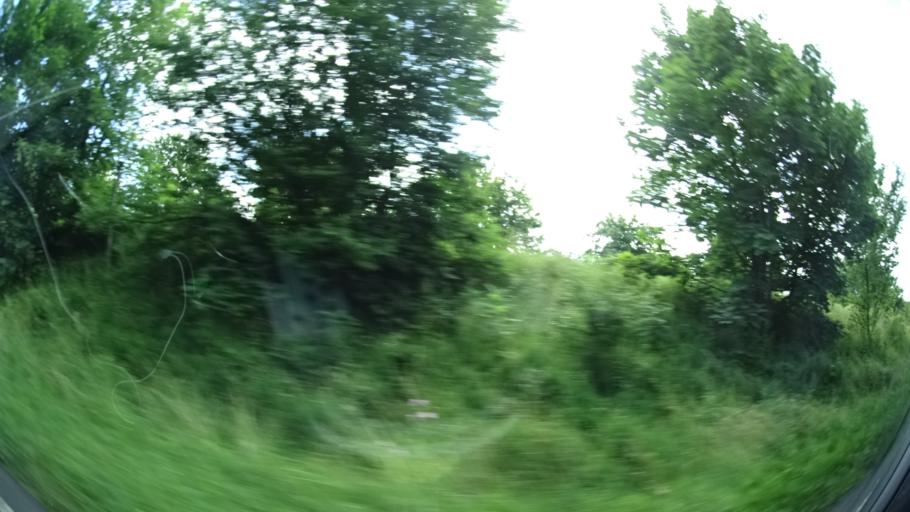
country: DK
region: Central Jutland
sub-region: Arhus Kommune
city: Beder
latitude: 56.0771
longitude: 10.2089
